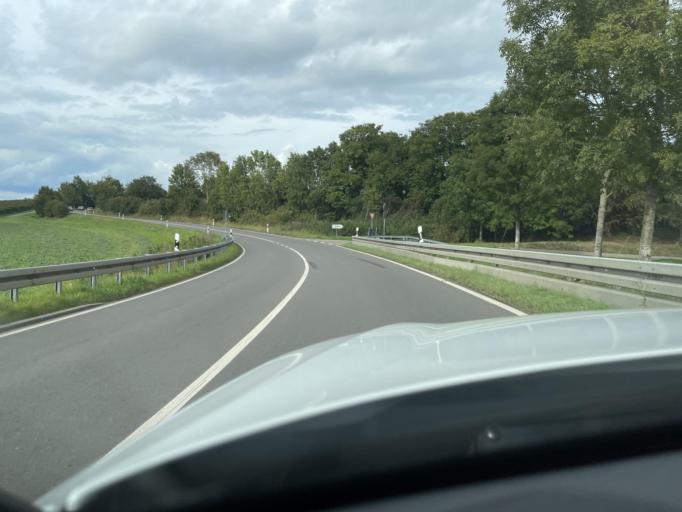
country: DE
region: Baden-Wuerttemberg
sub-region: Regierungsbezirk Stuttgart
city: Marbach am Neckar
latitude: 48.9248
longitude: 9.2697
